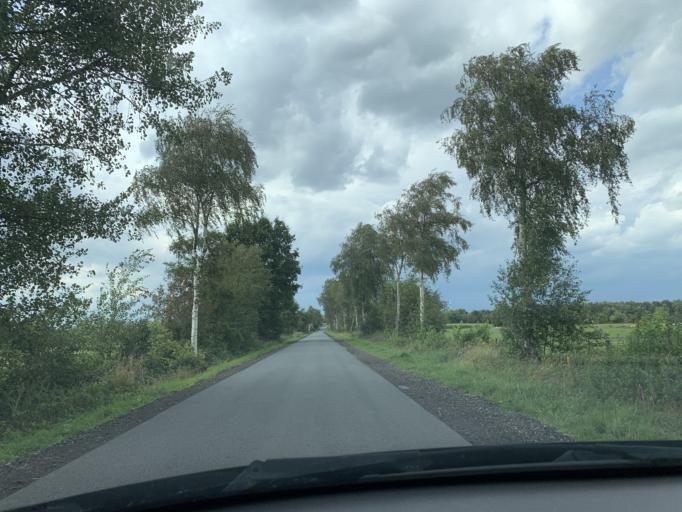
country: DE
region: Lower Saxony
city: Apen
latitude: 53.2738
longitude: 7.8236
